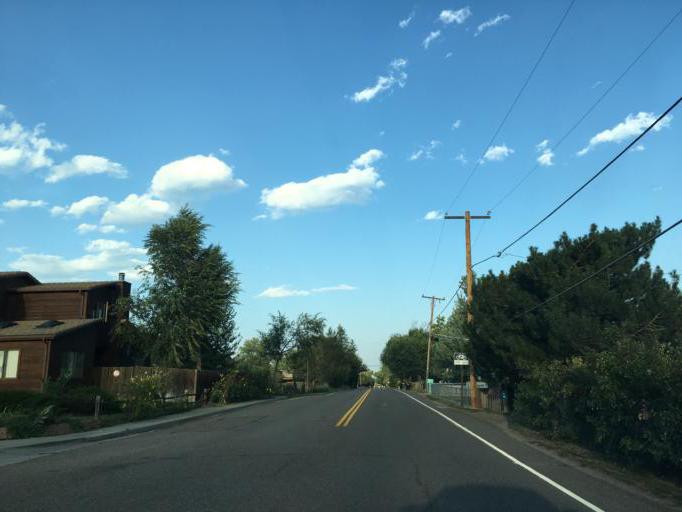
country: US
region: Colorado
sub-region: Jefferson County
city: Applewood
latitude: 39.7908
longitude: -105.1539
